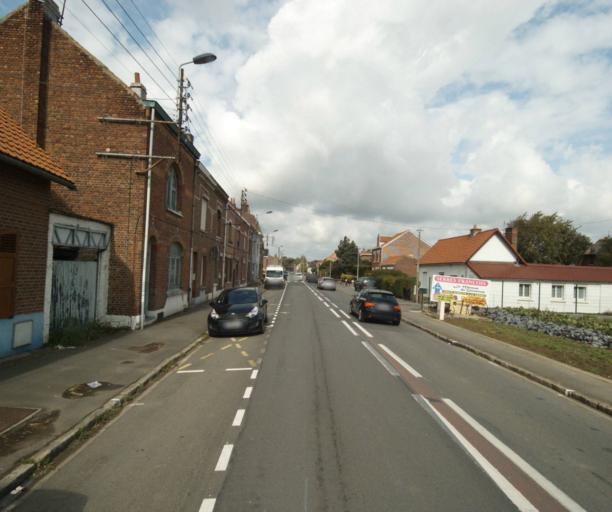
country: FR
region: Nord-Pas-de-Calais
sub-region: Departement du Nord
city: Perenchies
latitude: 50.6761
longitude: 2.9656
